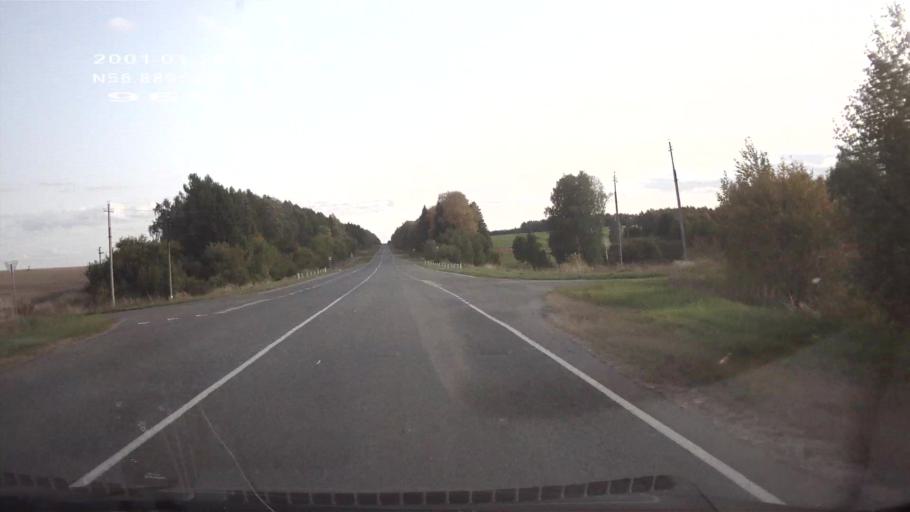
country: RU
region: Mariy-El
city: Kuzhener
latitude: 56.8882
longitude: 48.7518
